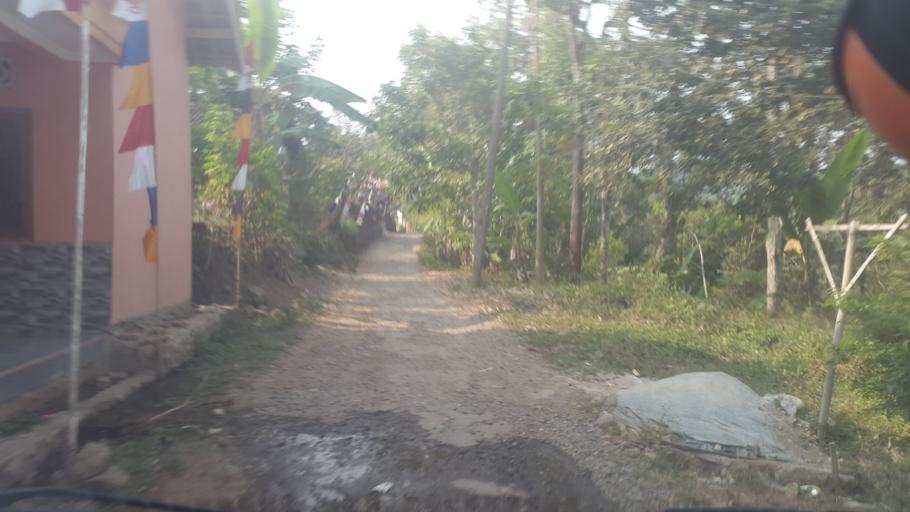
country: ID
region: West Java
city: Pelabuhanratu
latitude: -6.9391
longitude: 106.5509
